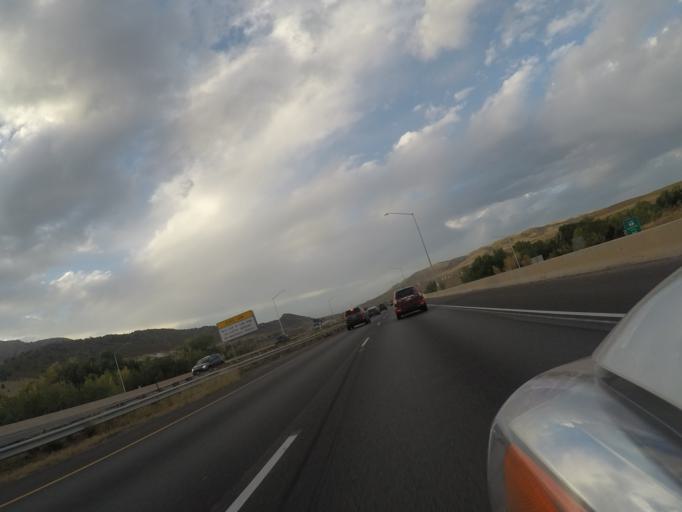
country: US
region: Colorado
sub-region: Jefferson County
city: Indian Hills
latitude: 39.6510
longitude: -105.1810
